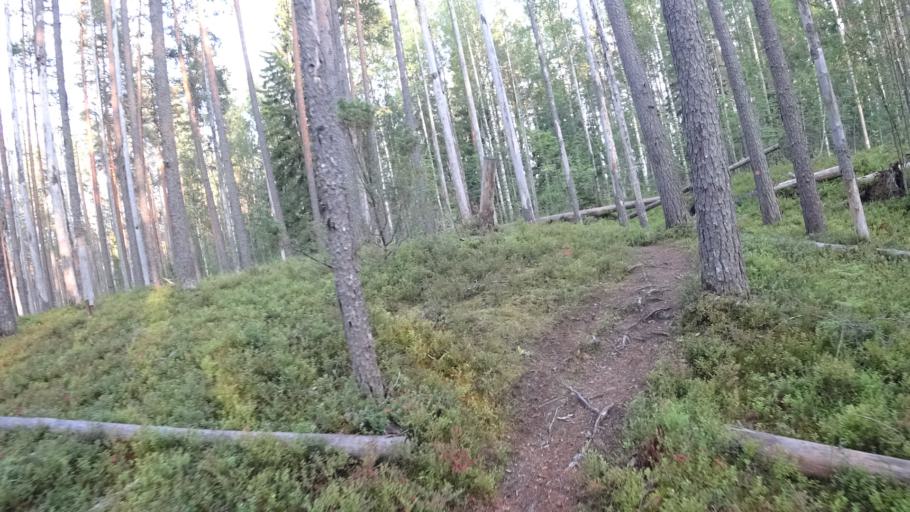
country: FI
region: North Karelia
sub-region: Joensuu
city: Ilomantsi
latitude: 62.5825
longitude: 31.1667
